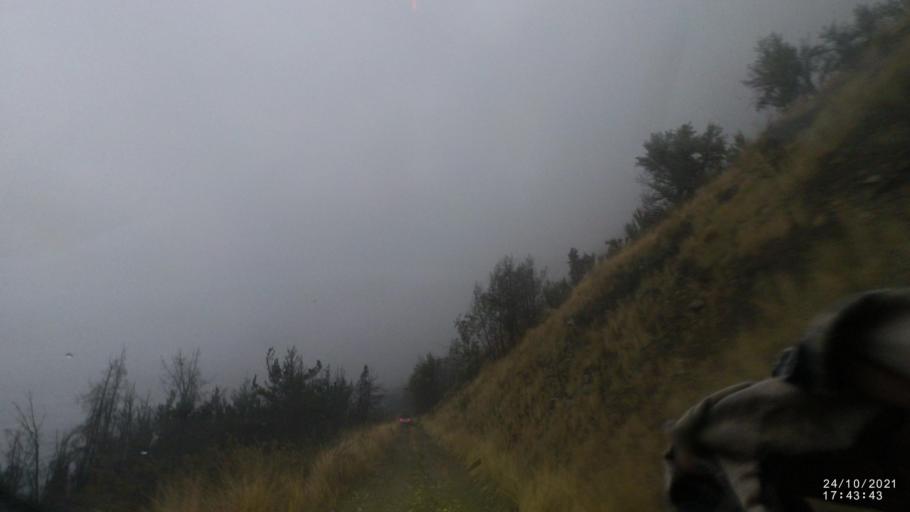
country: BO
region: Cochabamba
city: Cochabamba
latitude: -17.3151
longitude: -66.1330
